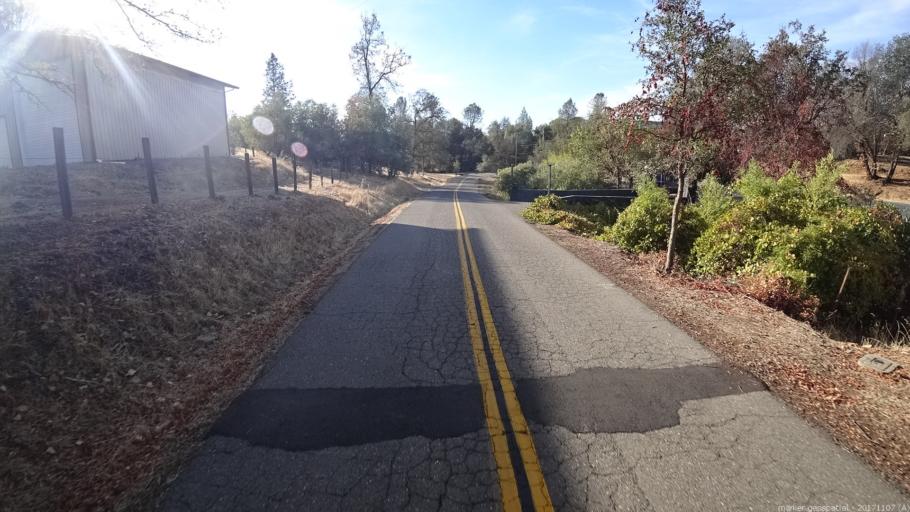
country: US
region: California
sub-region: Shasta County
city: Shasta
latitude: 40.5419
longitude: -122.4553
